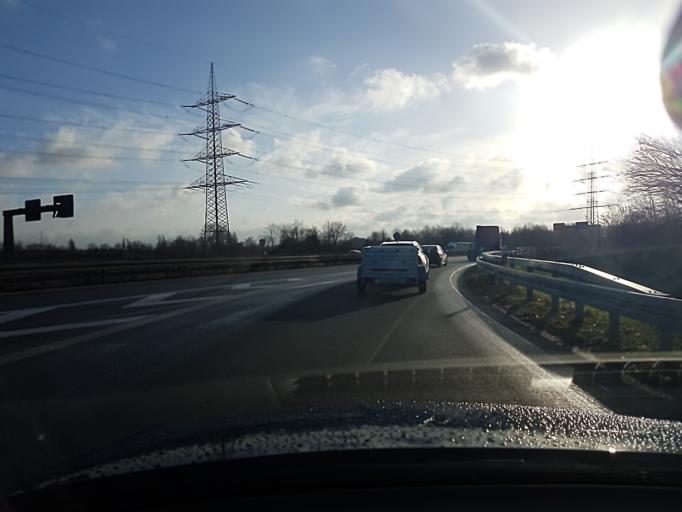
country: DE
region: North Rhine-Westphalia
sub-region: Regierungsbezirk Dusseldorf
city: Essen
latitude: 51.5063
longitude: 6.9957
